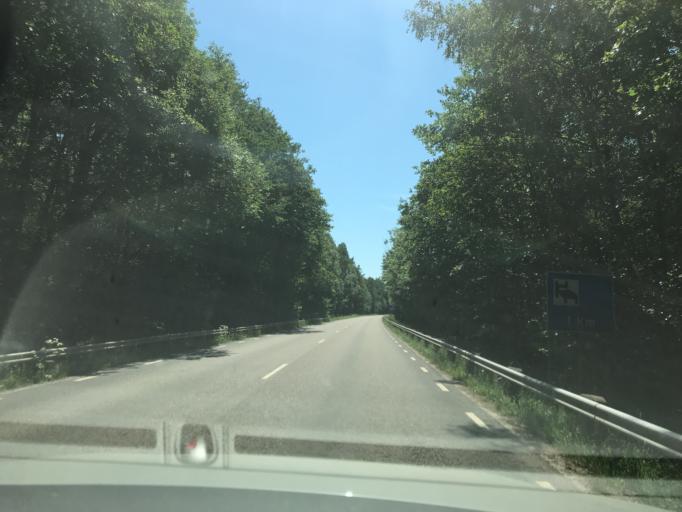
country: SE
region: Vaestra Goetaland
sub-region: Gotene Kommun
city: Kallby
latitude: 58.6054
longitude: 13.3981
